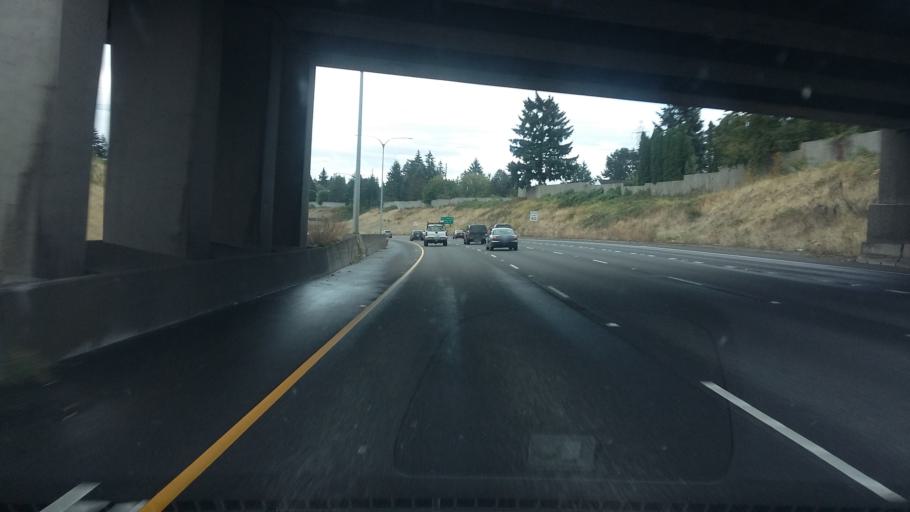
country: US
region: Washington
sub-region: Clark County
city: Hazel Dell
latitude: 45.6680
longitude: -122.6675
